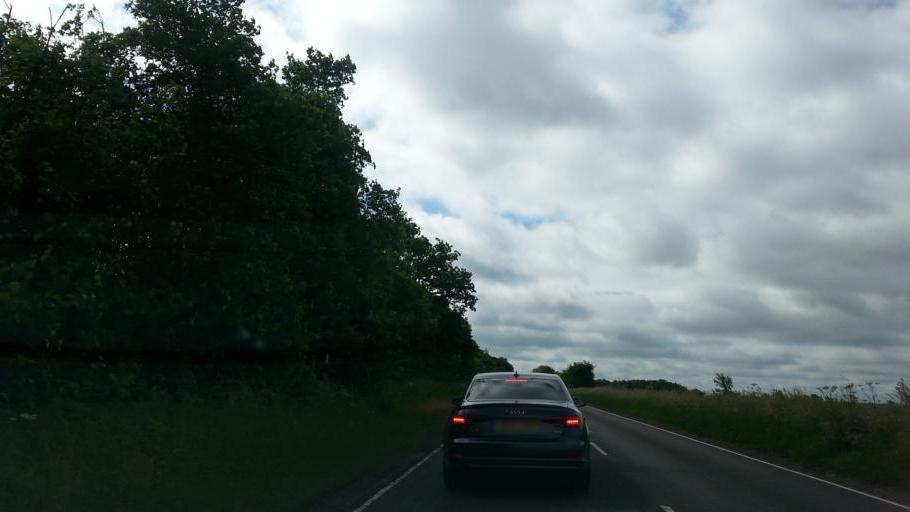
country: GB
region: England
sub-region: Cambridgeshire
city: Papworth Everard
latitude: 52.2342
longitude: -0.1070
